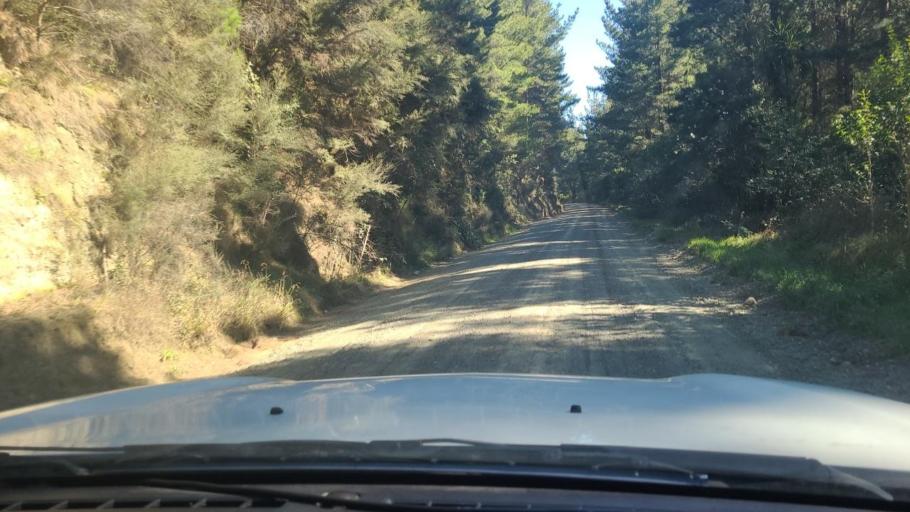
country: NZ
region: Hawke's Bay
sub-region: Napier City
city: Taradale
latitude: -39.4082
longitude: 176.4750
